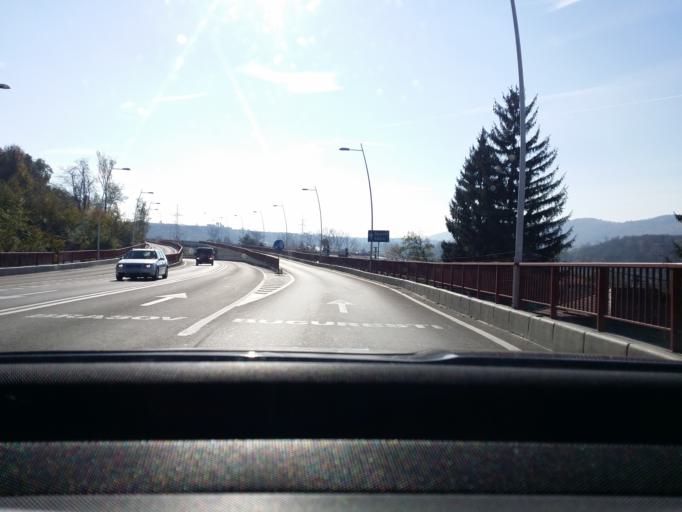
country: RO
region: Prahova
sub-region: Comuna Poiana Campina
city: Bobolia
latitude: 45.1082
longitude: 25.7454
